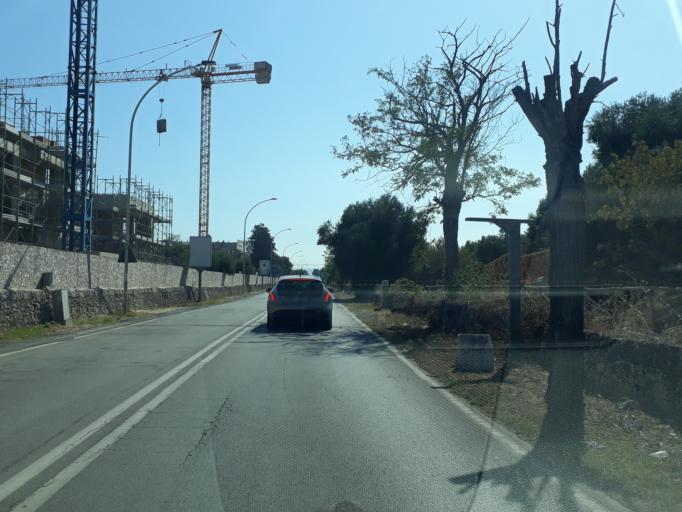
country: IT
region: Apulia
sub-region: Provincia di Bari
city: Monopoli
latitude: 40.9388
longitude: 17.3077
